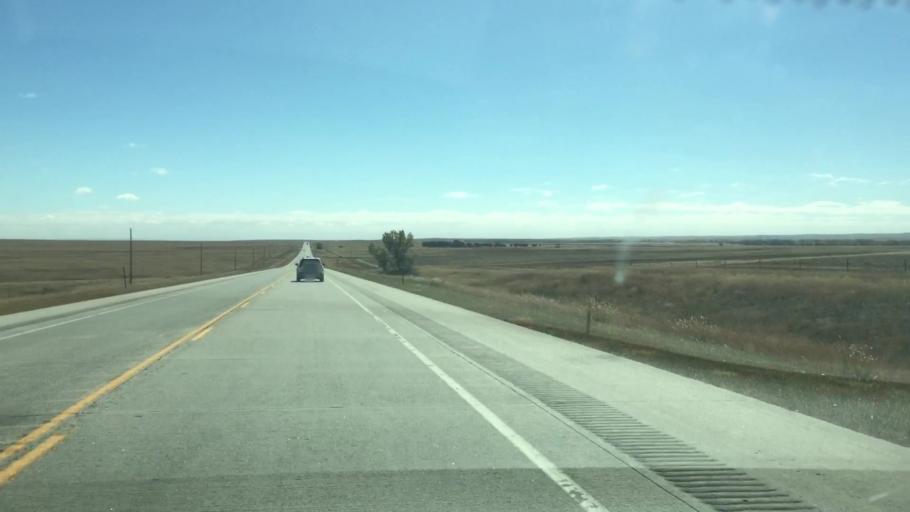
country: US
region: Colorado
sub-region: Lincoln County
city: Limon
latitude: 39.2076
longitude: -103.5917
